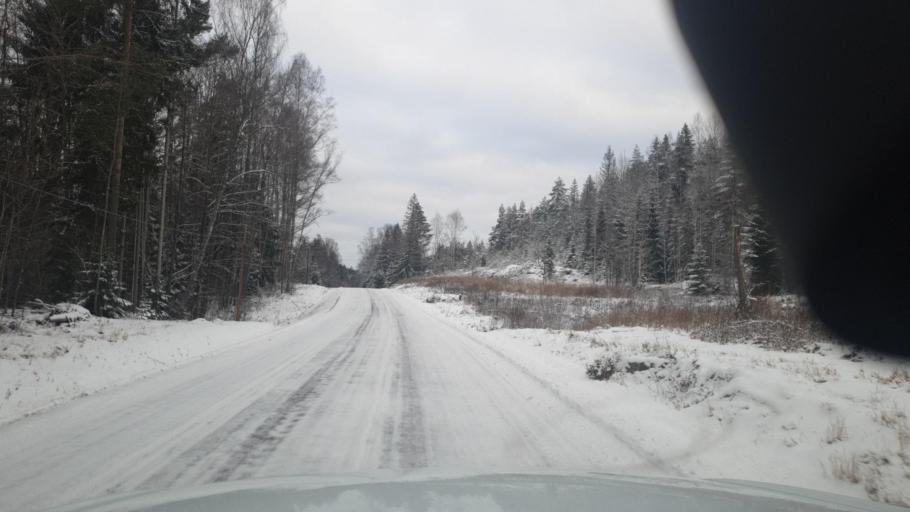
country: SE
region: Vaermland
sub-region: Grums Kommun
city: Grums
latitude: 59.4045
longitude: 13.0713
